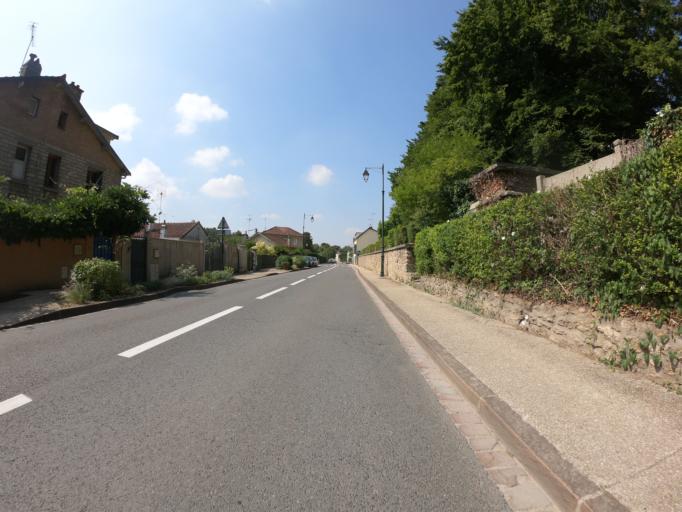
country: FR
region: Ile-de-France
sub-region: Departement de l'Essonne
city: Bievres
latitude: 48.7613
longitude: 2.2227
